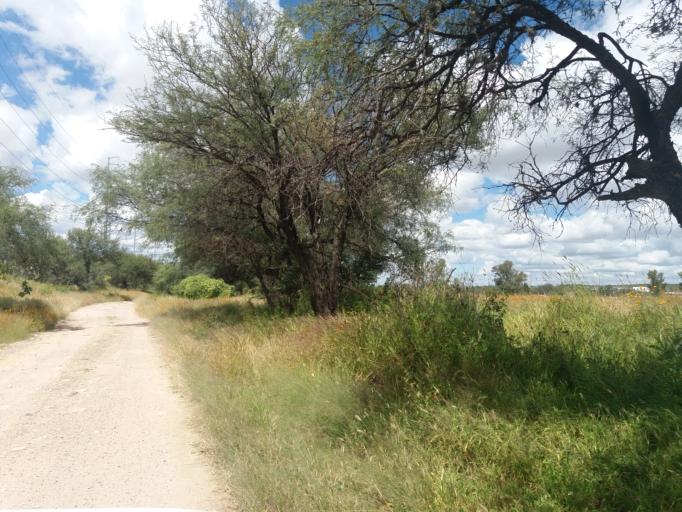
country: MX
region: Aguascalientes
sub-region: Aguascalientes
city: San Sebastian [Fraccionamiento]
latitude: 21.8139
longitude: -102.2707
